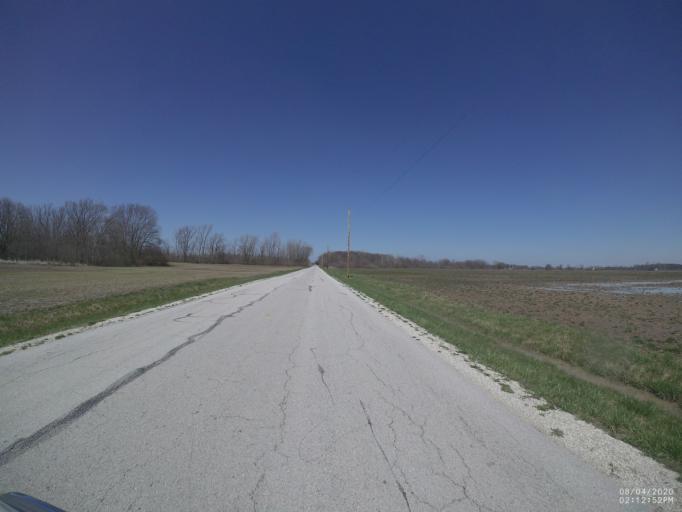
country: US
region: Ohio
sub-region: Sandusky County
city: Gibsonburg
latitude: 41.2549
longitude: -83.2646
